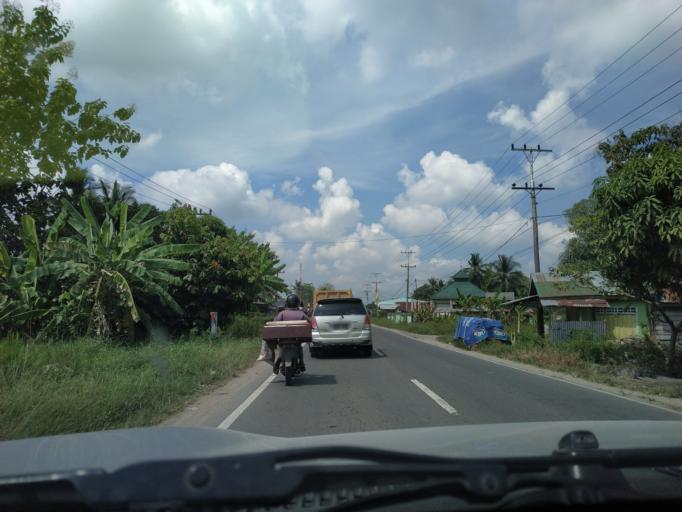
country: ID
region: North Sumatra
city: Tanjungbalai
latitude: 2.9257
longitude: 99.7380
